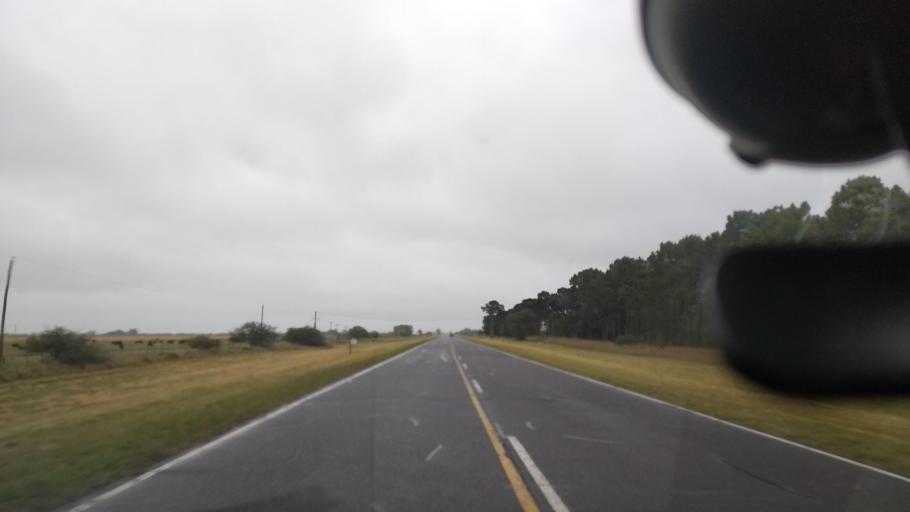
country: AR
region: Buenos Aires
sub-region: Partido de Dolores
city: Dolores
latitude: -36.0496
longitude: -57.4443
